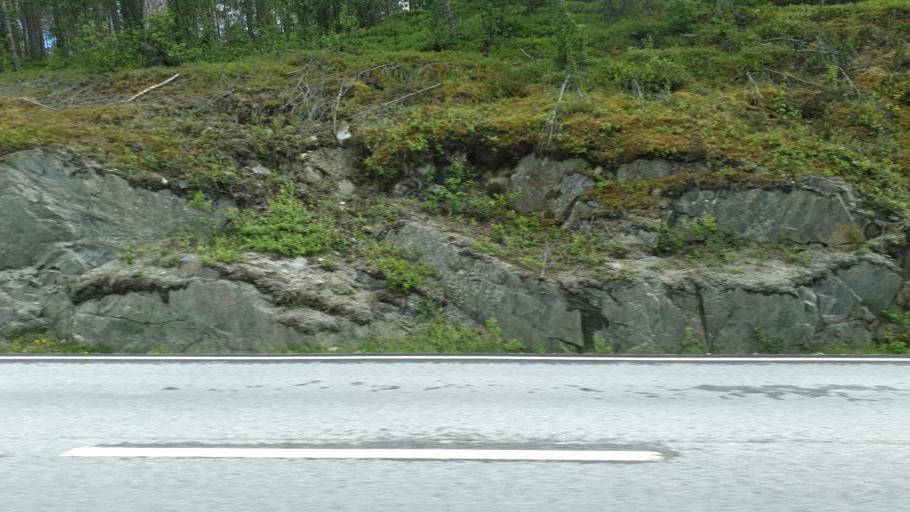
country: NO
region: Oppland
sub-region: Dovre
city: Dombas
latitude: 62.0856
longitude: 9.1517
